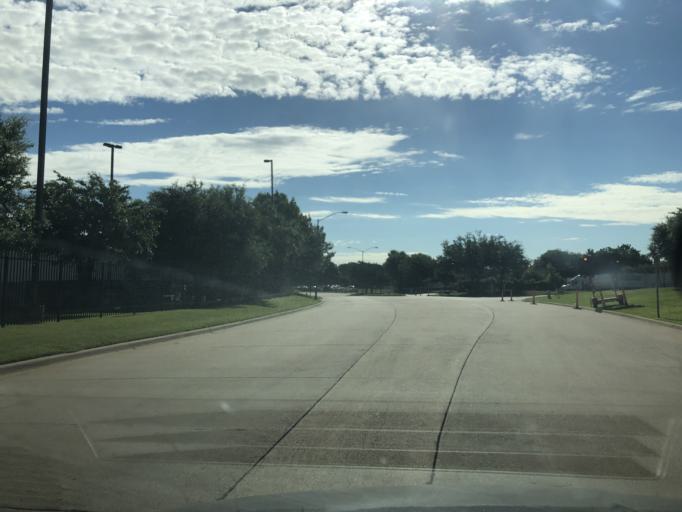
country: US
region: Texas
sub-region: Tarrant County
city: Euless
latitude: 32.8196
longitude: -97.0420
